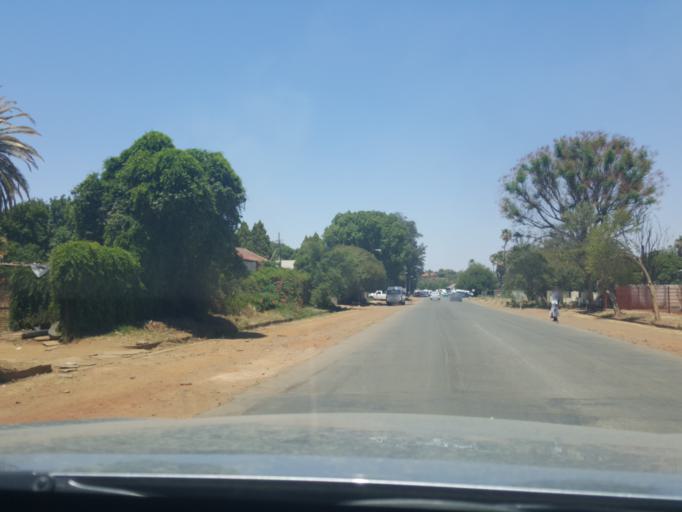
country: ZA
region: North-West
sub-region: Ngaka Modiri Molema District Municipality
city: Zeerust
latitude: -25.5428
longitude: 26.0738
